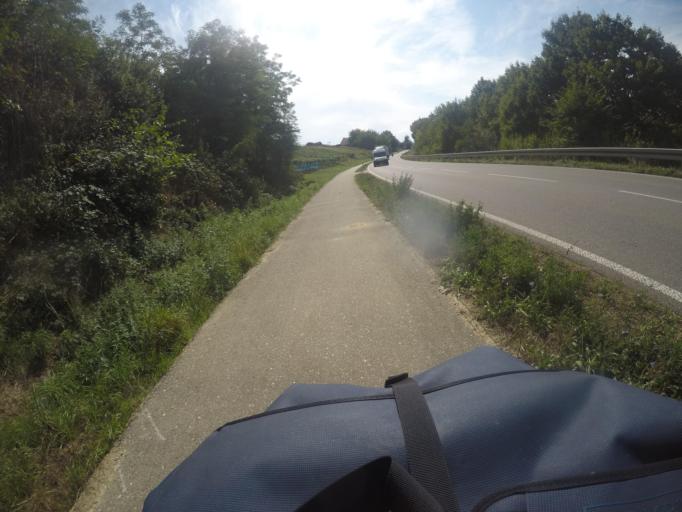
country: DE
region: Baden-Wuerttemberg
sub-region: Freiburg Region
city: Bad Bellingen
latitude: 47.7128
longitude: 7.5381
